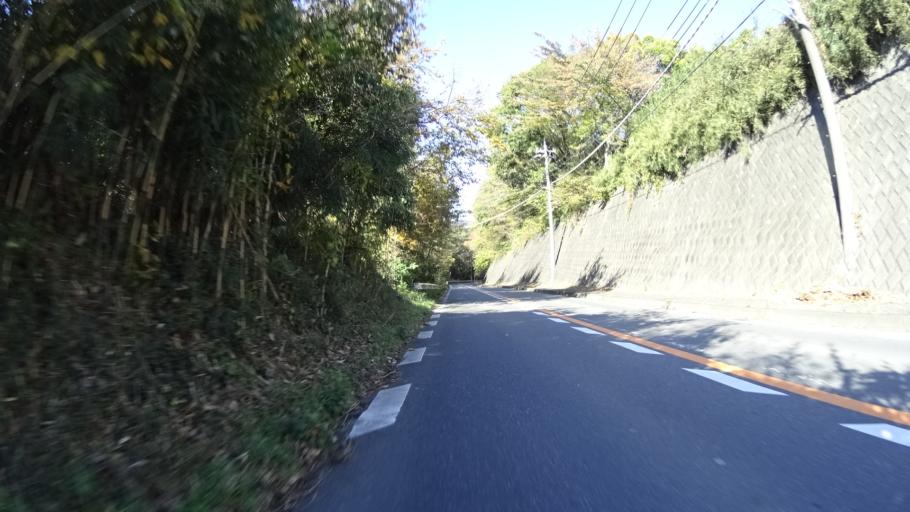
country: JP
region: Kanagawa
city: Zama
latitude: 35.5294
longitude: 139.3151
